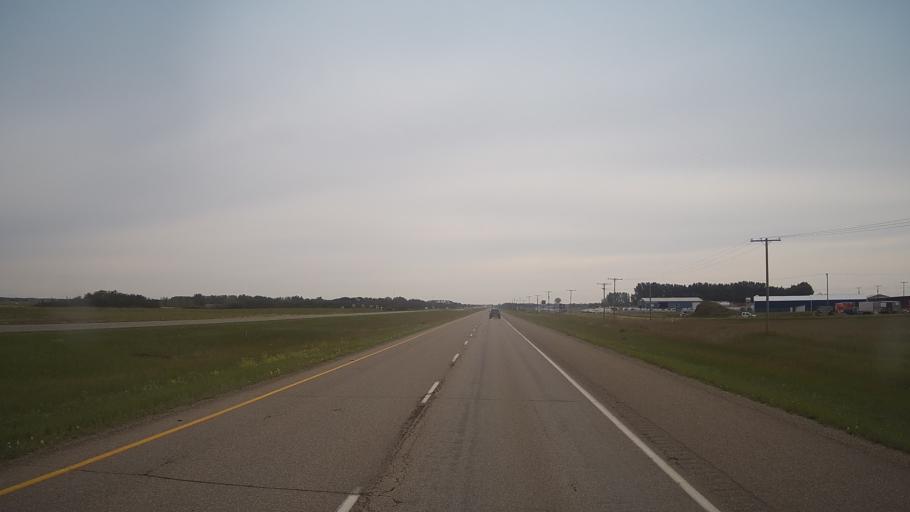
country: CA
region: Saskatchewan
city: Saskatoon
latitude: 51.9633
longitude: -106.5504
